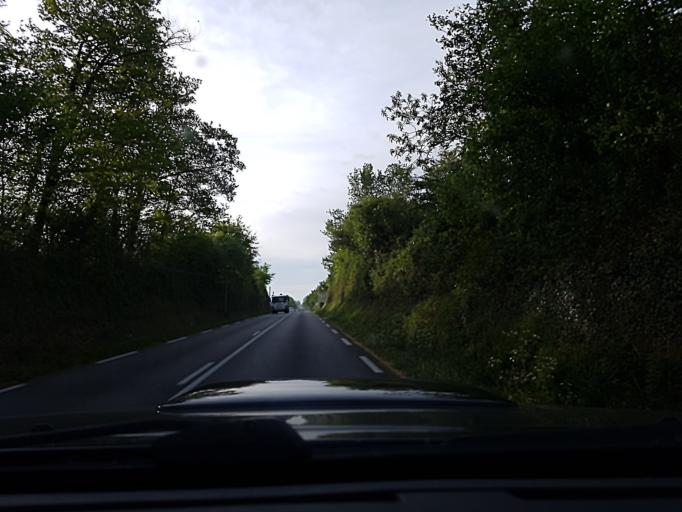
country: FR
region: Pays de la Loire
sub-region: Departement de la Vendee
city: Aizenay
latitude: 46.7533
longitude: -1.6338
